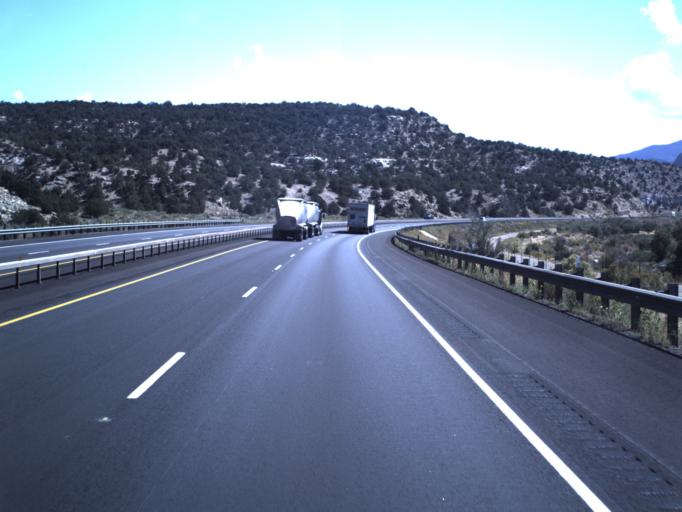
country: US
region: Utah
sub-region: Sevier County
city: Salina
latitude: 38.9157
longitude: -111.7234
